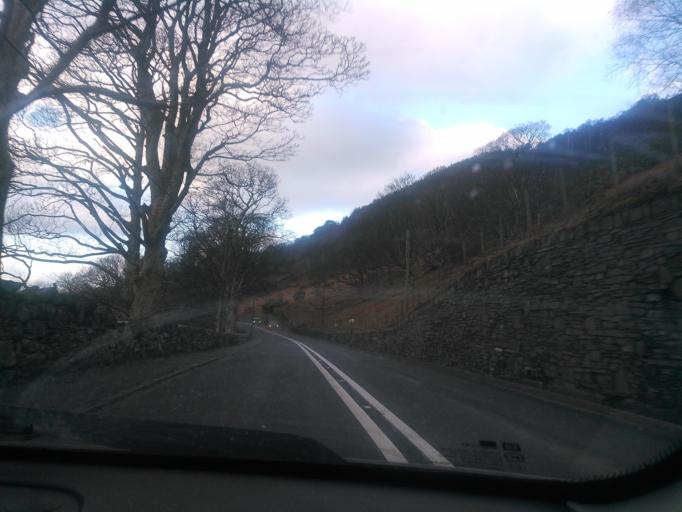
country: GB
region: Wales
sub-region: Gwynedd
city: Bethesda
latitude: 53.1641
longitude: -4.0465
